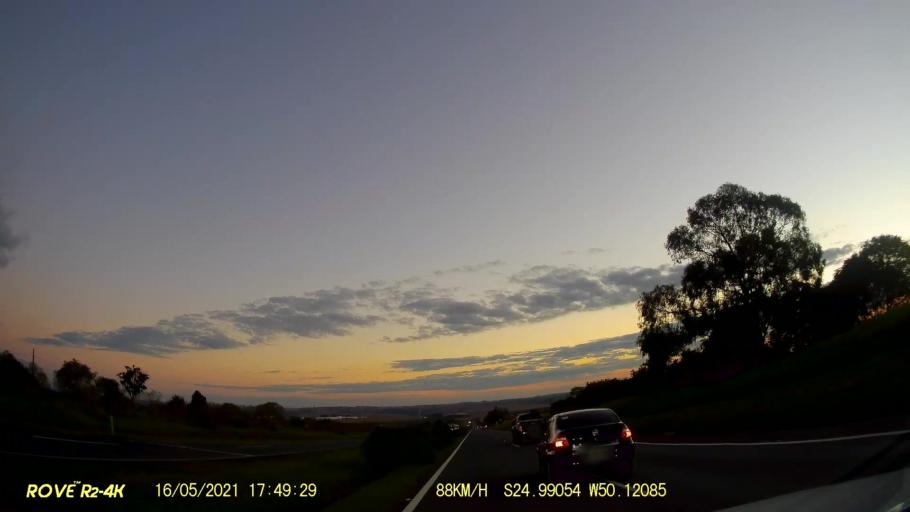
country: BR
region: Parana
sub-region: Carambei
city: Carambei
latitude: -24.9907
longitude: -50.1211
